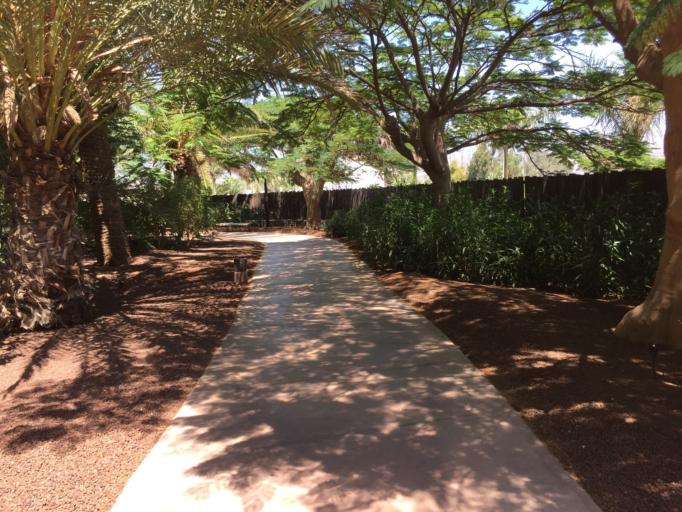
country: ES
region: Canary Islands
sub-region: Provincia de Las Palmas
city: Maspalomas
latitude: 27.7425
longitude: -15.5995
